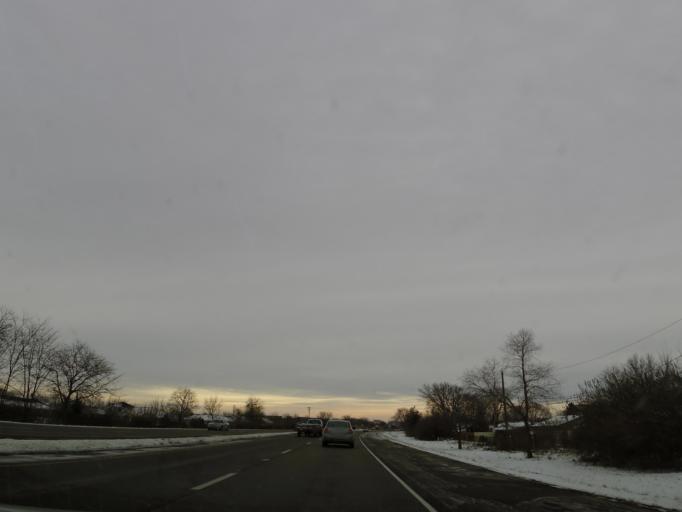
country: US
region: Illinois
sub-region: LaSalle County
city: Peru
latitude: 41.3430
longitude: -89.1211
